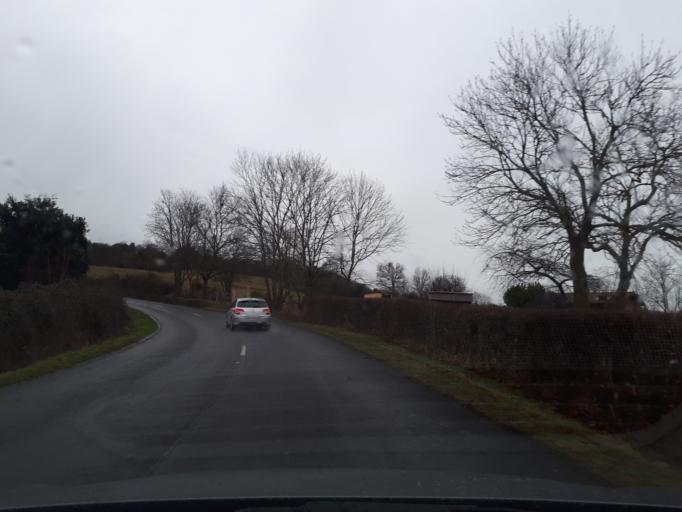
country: FR
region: Rhone-Alpes
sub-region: Departement de la Loire
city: Boen-sur-Lignon
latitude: 45.7757
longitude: 3.9932
